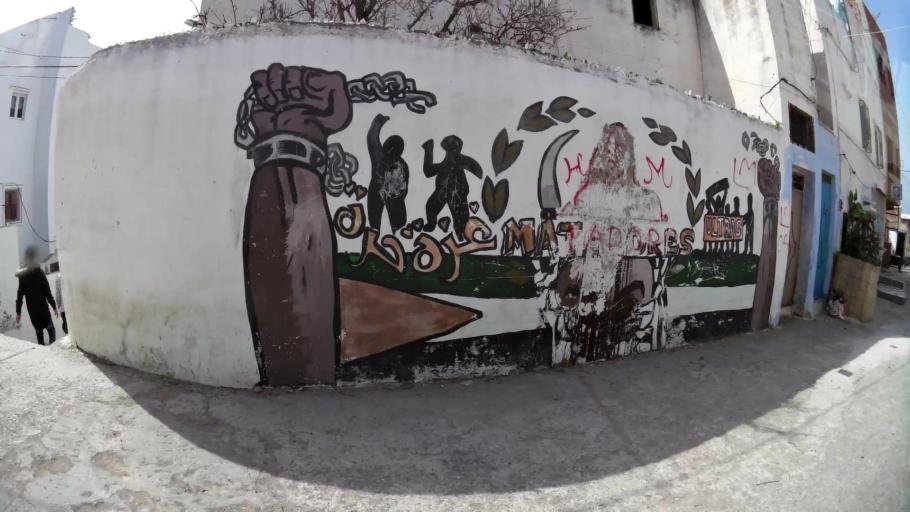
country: MA
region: Tanger-Tetouan
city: Tetouan
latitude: 35.5760
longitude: -5.3850
